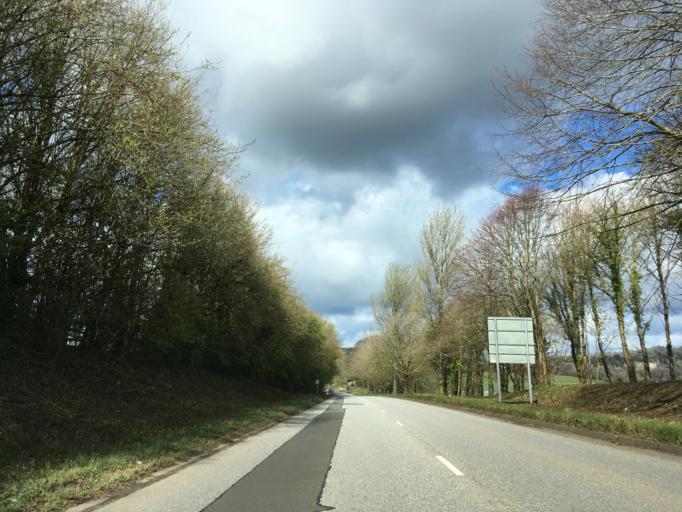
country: GB
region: Wales
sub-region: Monmouthshire
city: Chepstow
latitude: 51.6561
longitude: -2.6927
